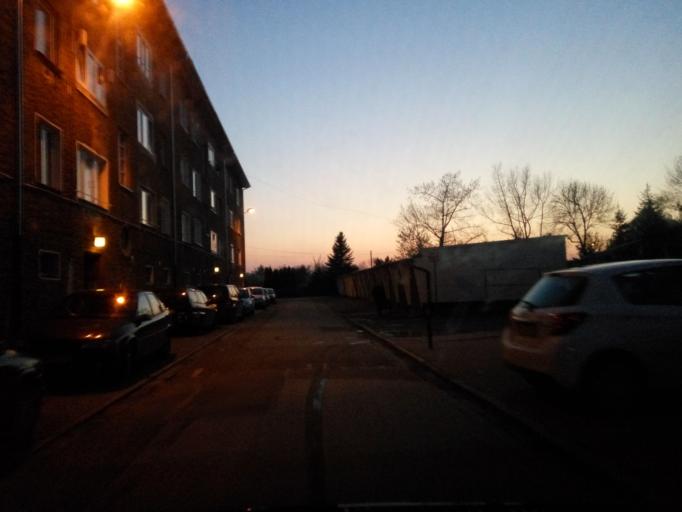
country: PL
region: Lower Silesian Voivodeship
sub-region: Powiat wroclawski
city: Radwanice
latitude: 51.0728
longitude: 17.0847
